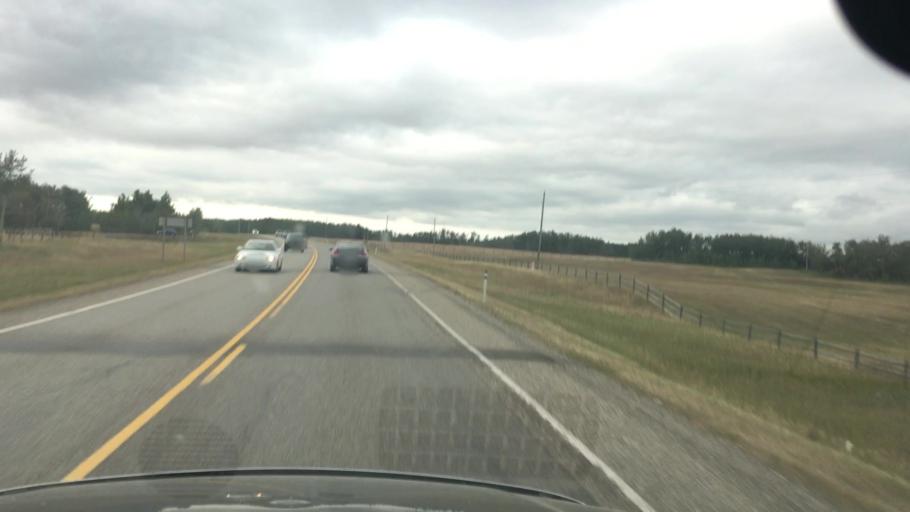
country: CA
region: Alberta
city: Cochrane
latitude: 51.3560
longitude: -114.4769
